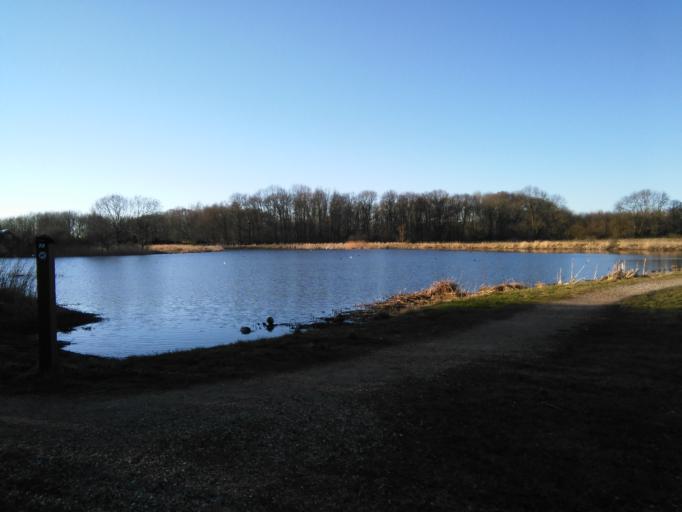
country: DK
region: Central Jutland
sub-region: Arhus Kommune
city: Malling
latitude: 56.0449
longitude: 10.2025
